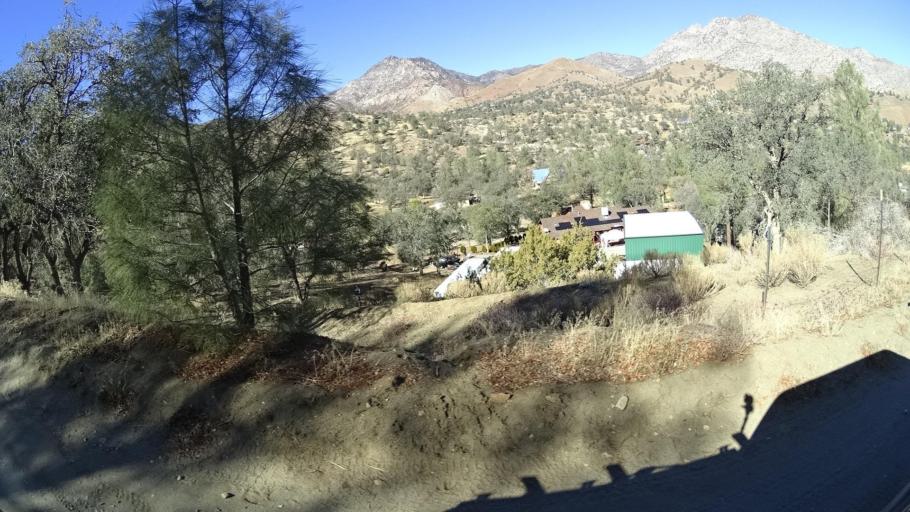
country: US
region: California
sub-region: Kern County
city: Wofford Heights
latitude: 35.7055
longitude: -118.4754
